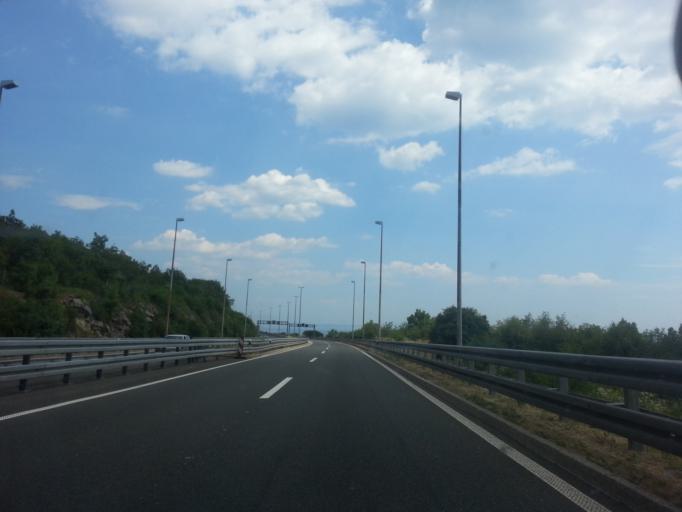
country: HR
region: Primorsko-Goranska
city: Rubesi
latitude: 45.3515
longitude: 14.3600
